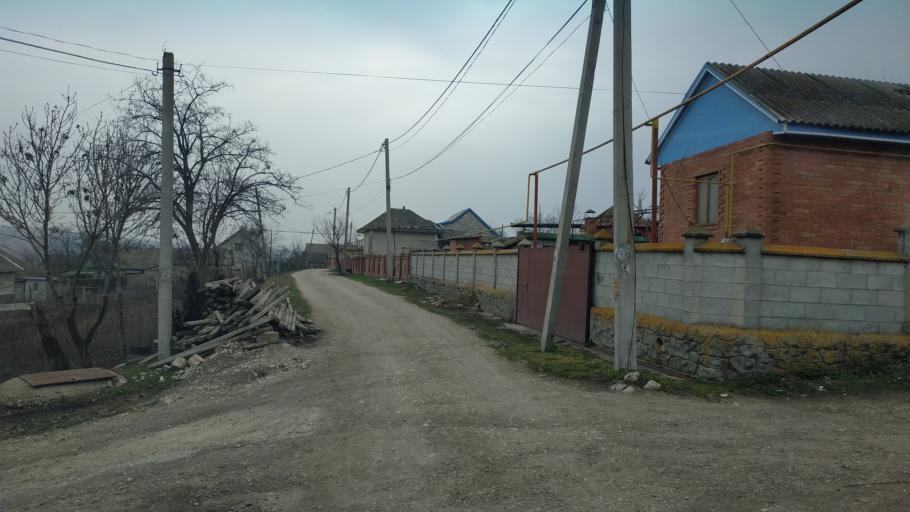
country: MD
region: Chisinau
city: Singera
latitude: 46.8276
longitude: 29.0307
